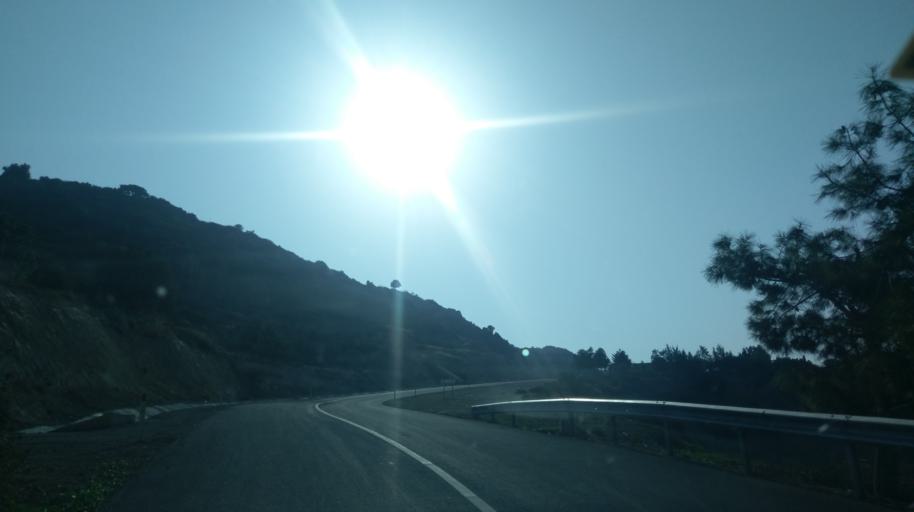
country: CY
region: Ammochostos
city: Rizokarpaso
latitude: 35.5252
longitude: 34.2981
